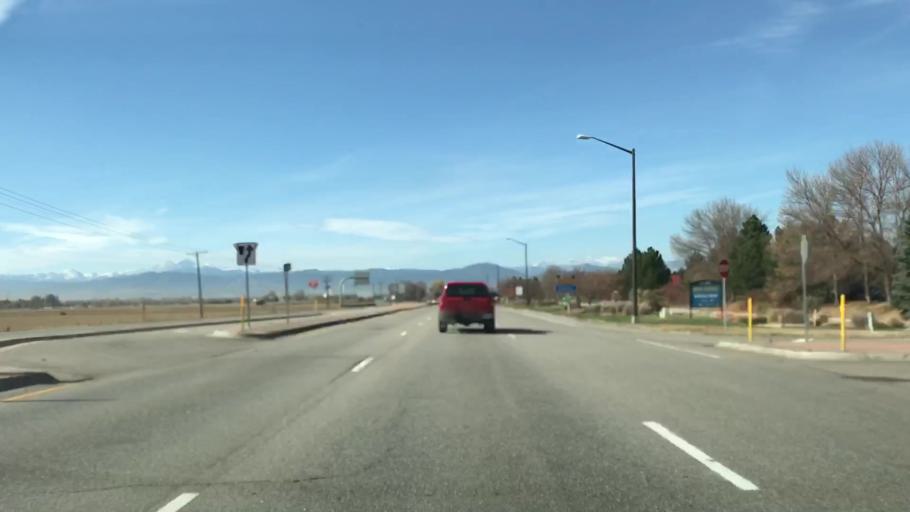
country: US
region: Colorado
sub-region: Larimer County
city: Loveland
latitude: 40.4063
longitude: -104.9976
